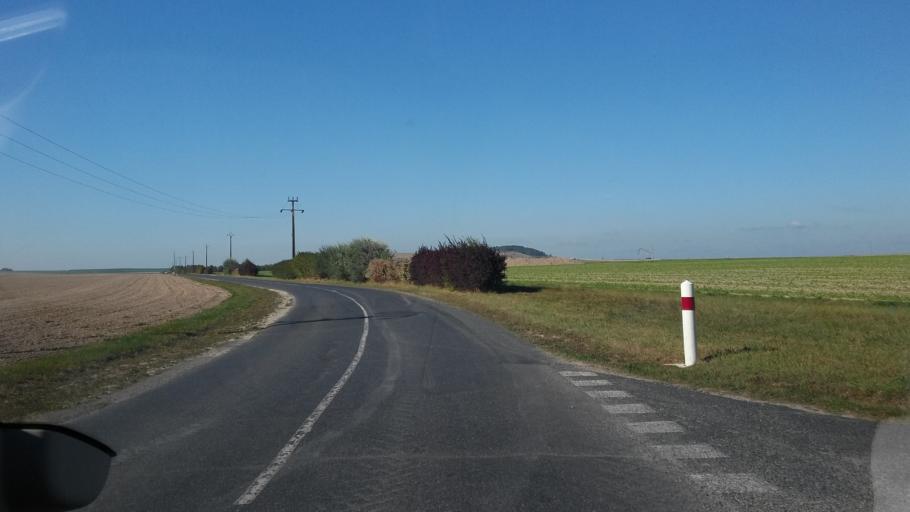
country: FR
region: Champagne-Ardenne
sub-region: Departement de la Marne
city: Connantre
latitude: 48.7321
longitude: 3.9059
